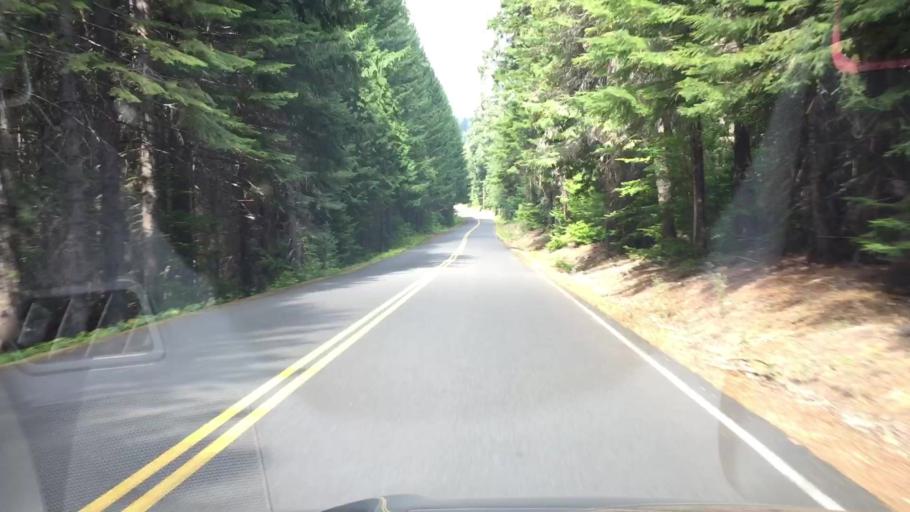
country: US
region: Washington
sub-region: Klickitat County
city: White Salmon
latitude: 46.0673
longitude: -121.5740
